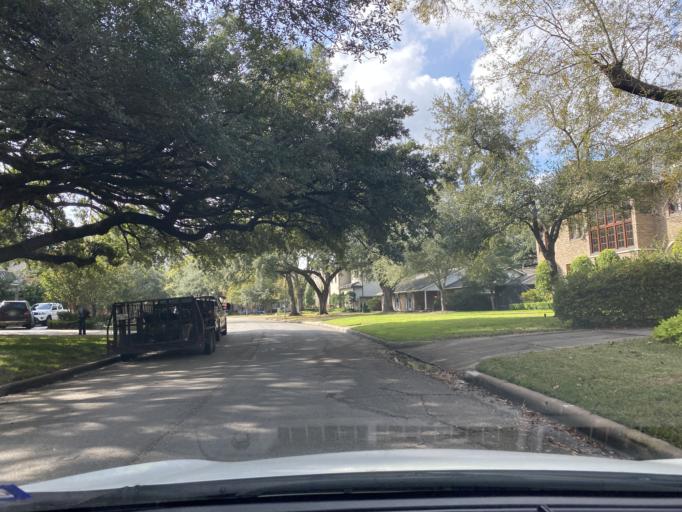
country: US
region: Texas
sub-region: Harris County
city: Hunters Creek Village
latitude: 29.7516
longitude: -95.4675
